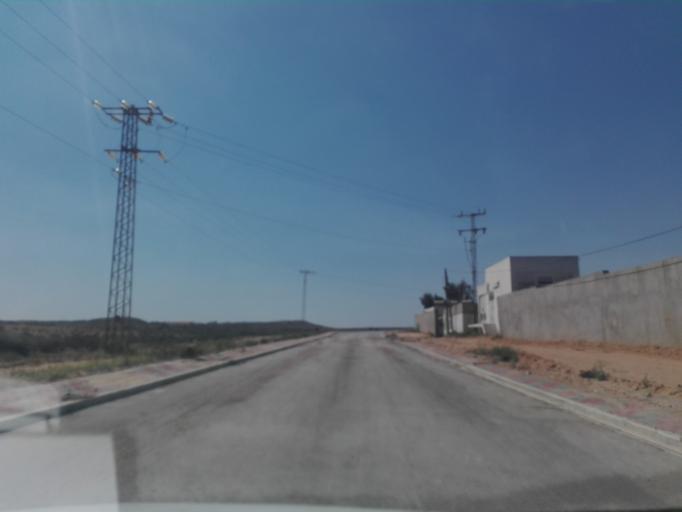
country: TN
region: Safaqis
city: Sfax
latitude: 34.7241
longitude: 10.5228
